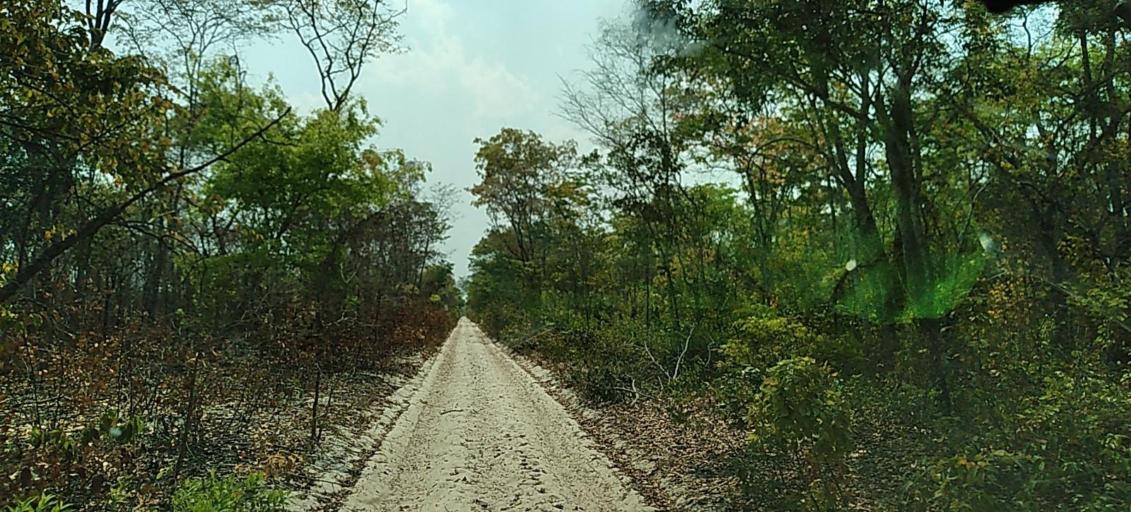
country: ZM
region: North-Western
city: Kabompo
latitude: -13.3938
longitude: 23.7927
